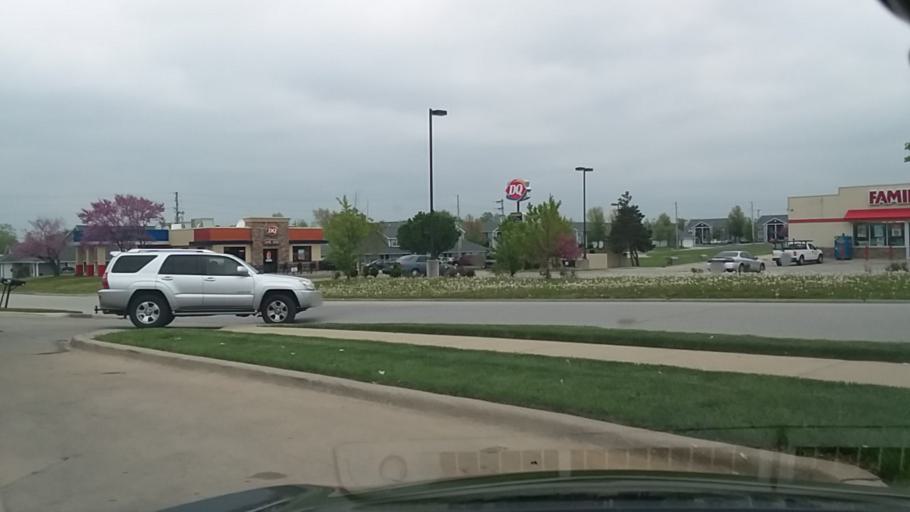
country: US
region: Kansas
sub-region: Douglas County
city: Eudora
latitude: 38.9336
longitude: -95.0956
